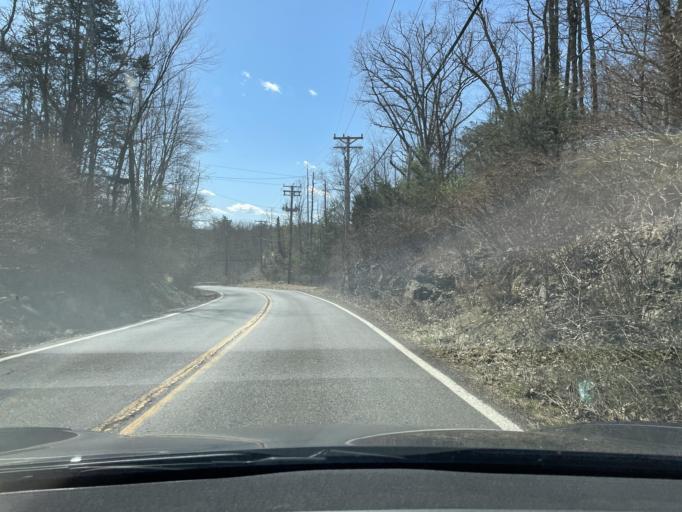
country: US
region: New York
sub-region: Ulster County
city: West Hurley
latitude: 41.9802
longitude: -74.0928
